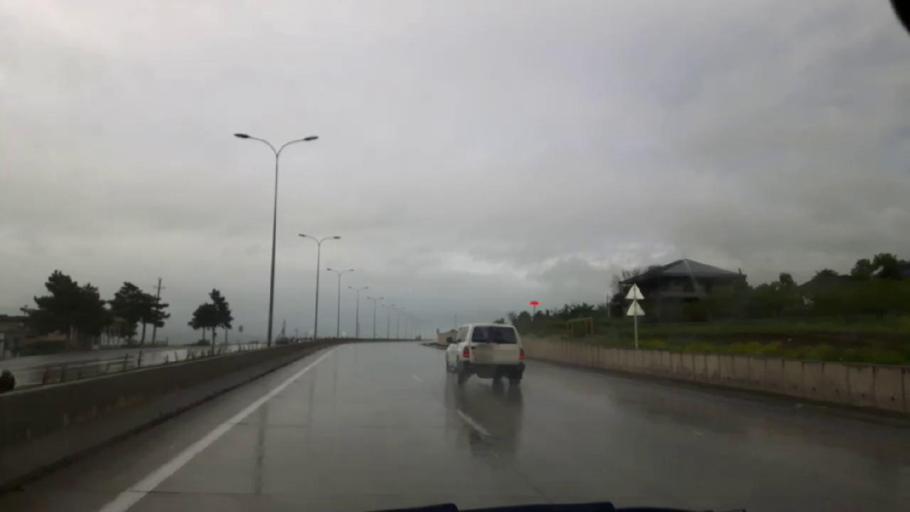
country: GE
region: Shida Kartli
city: Gori
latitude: 42.0263
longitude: 44.2001
